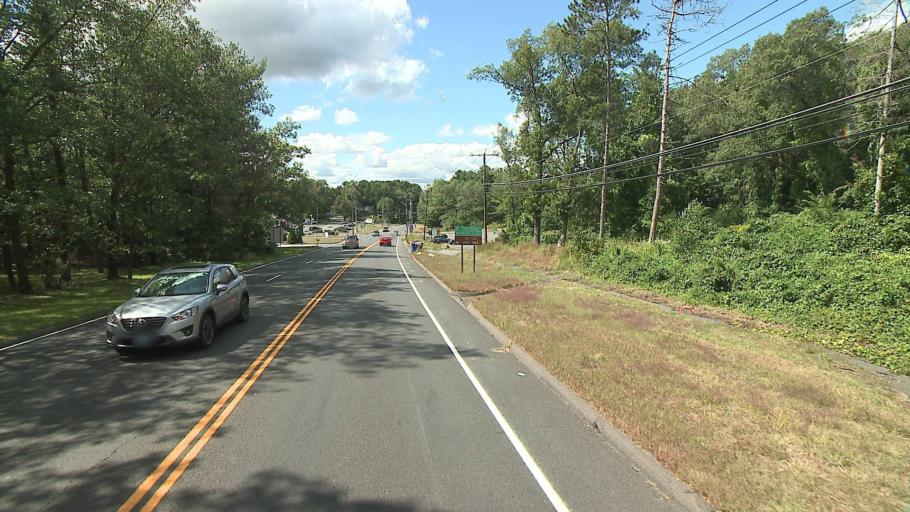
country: US
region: Connecticut
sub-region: Hartford County
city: Manchester
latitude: 41.7840
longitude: -72.4641
